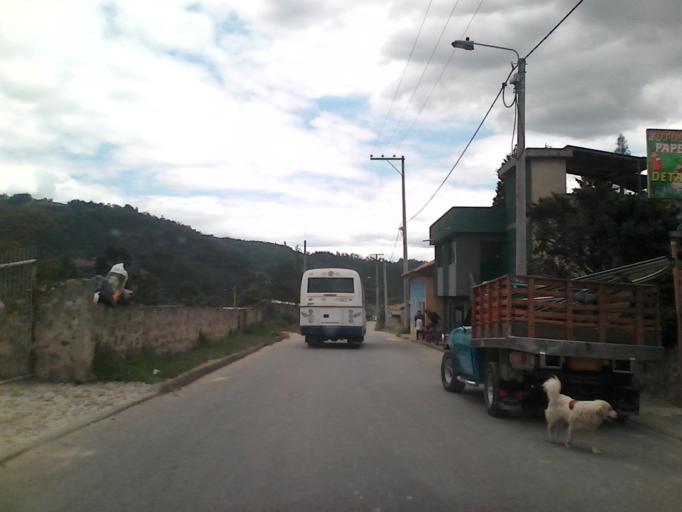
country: CO
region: Boyaca
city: Duitama
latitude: 5.8253
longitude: -73.0757
